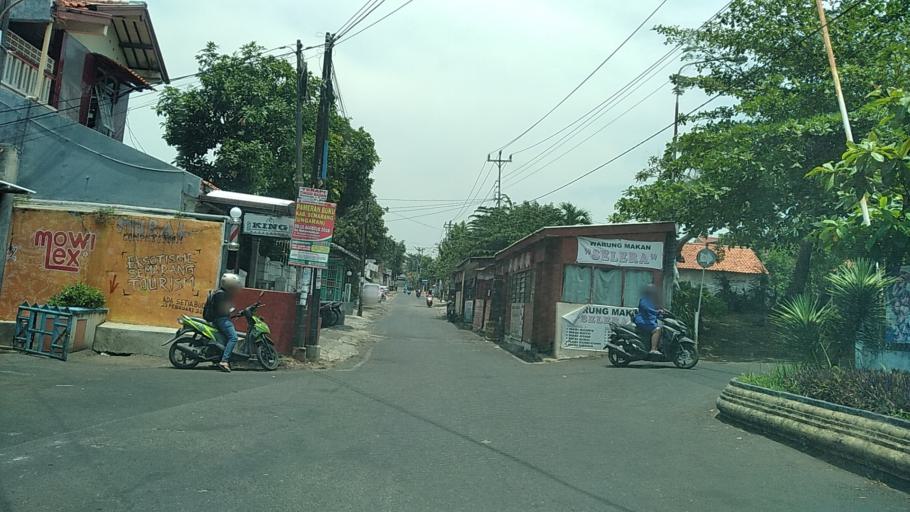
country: ID
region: Central Java
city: Semarang
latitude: -7.0604
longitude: 110.4133
